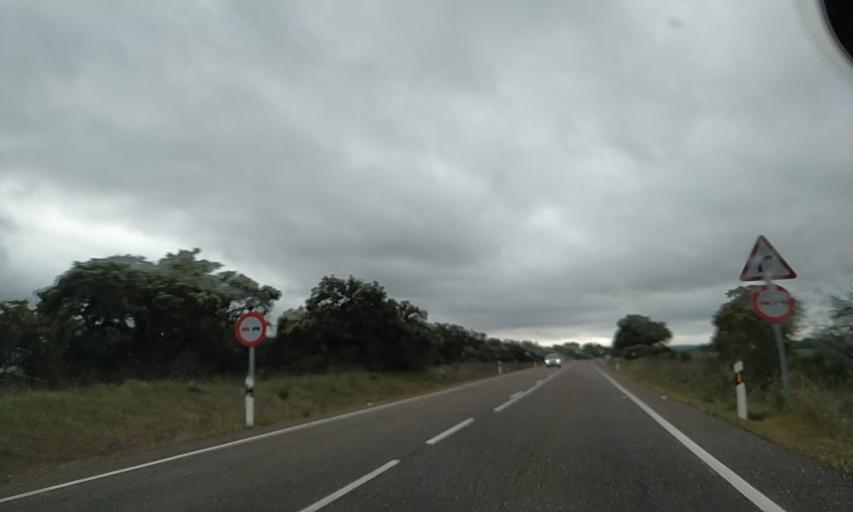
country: ES
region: Extremadura
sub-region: Provincia de Badajoz
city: La Roca de la Sierra
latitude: 39.0821
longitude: -6.7400
